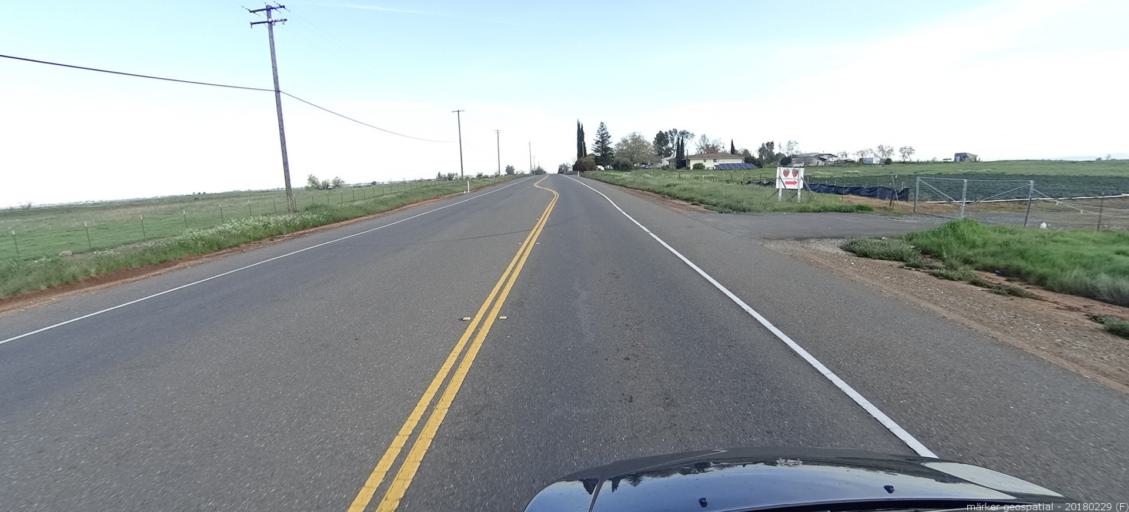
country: US
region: California
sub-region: Sacramento County
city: Rancho Cordova
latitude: 38.5196
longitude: -121.2979
